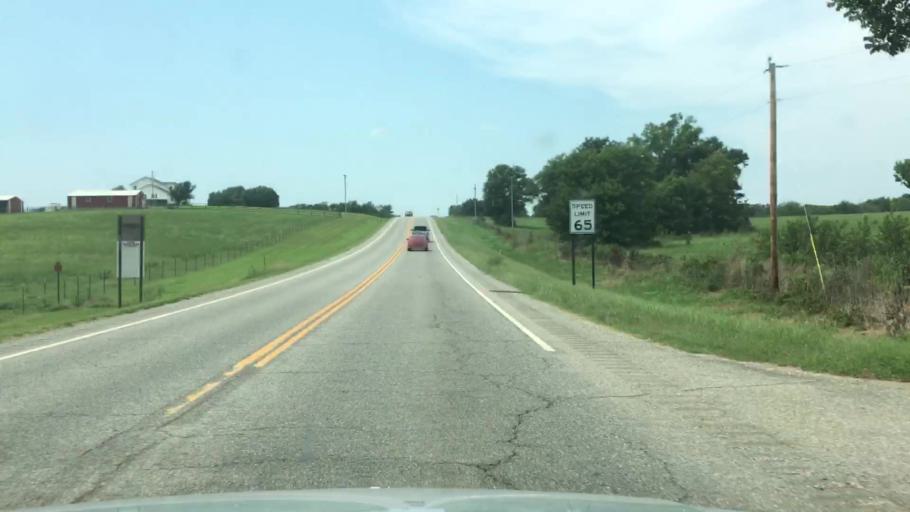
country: US
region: Oklahoma
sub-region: Muskogee County
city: Fort Gibson
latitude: 35.9369
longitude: -95.1901
